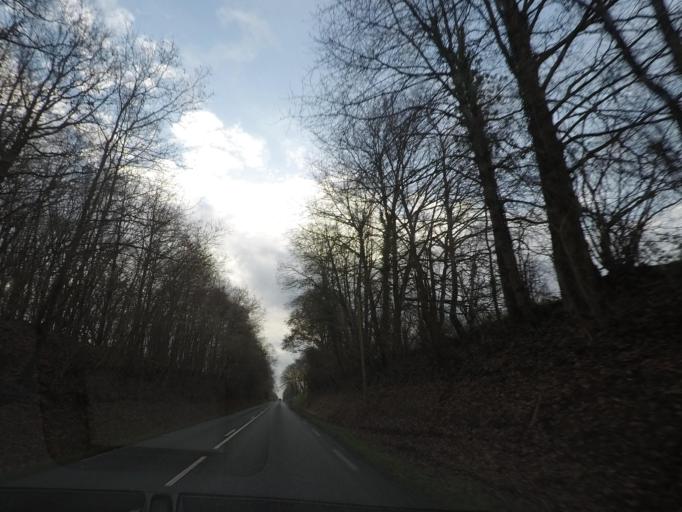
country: FR
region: Pays de la Loire
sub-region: Departement de la Sarthe
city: Cherre
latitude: 48.1396
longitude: 0.6927
